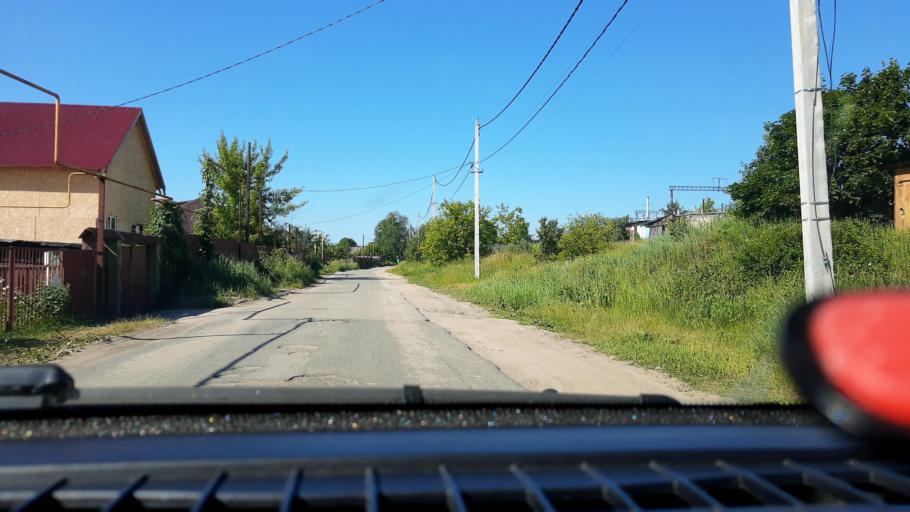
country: RU
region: Nizjnij Novgorod
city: Gidrotorf
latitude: 56.5107
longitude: 43.5353
